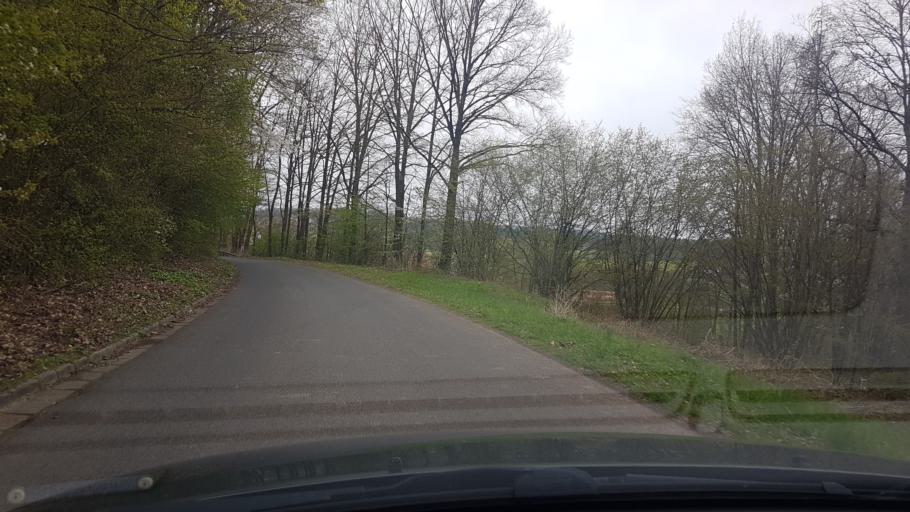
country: DE
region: Bavaria
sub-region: Regierungsbezirk Unterfranken
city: Rentweinsdorf
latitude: 50.0502
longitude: 10.8182
